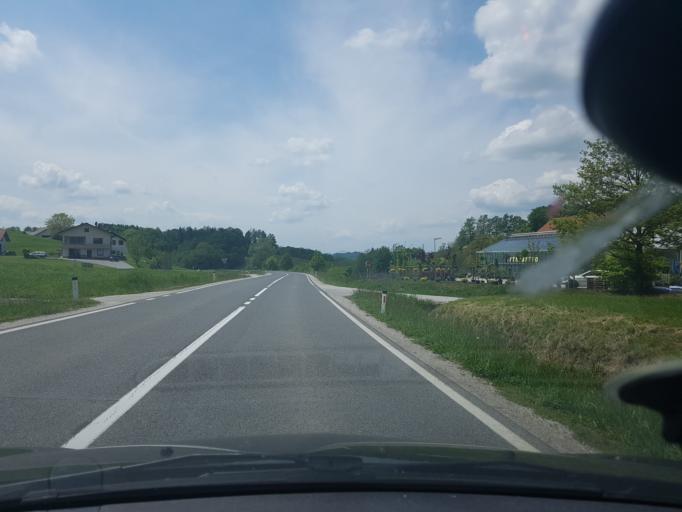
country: SI
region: Rogaska Slatina
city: Rogaska Slatina
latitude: 46.2516
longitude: 15.6081
